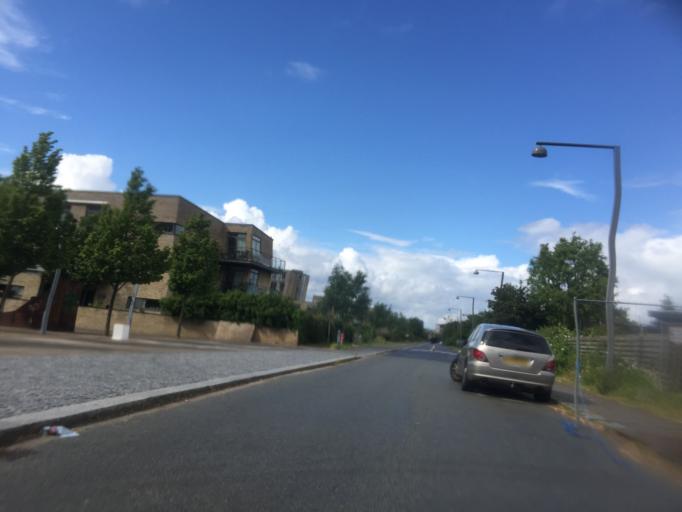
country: DK
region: Capital Region
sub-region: Tarnby Kommune
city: Tarnby
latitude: 55.6449
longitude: 12.5870
